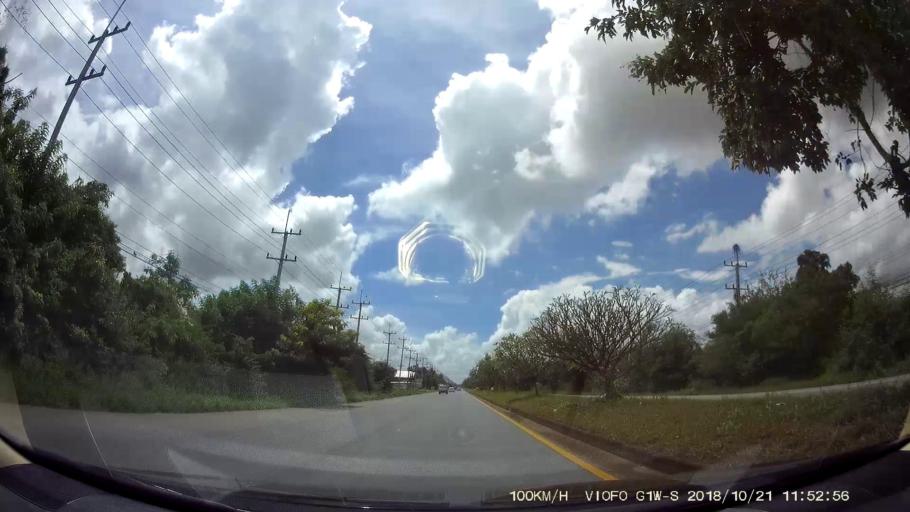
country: TH
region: Chaiyaphum
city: Chatturat
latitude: 15.6024
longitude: 101.9087
